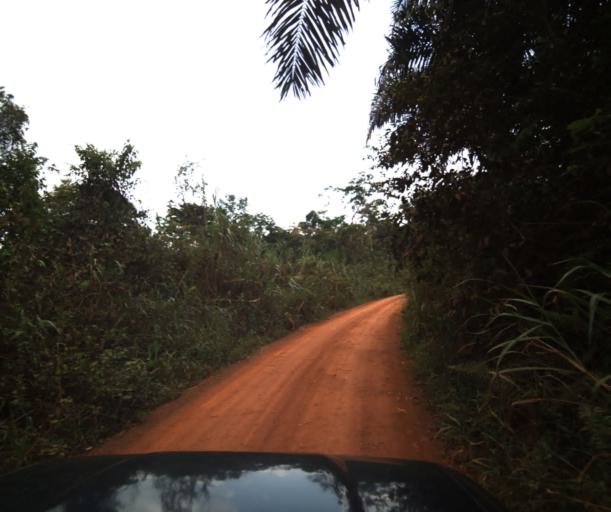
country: CM
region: Centre
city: Akono
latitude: 3.5968
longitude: 11.1711
